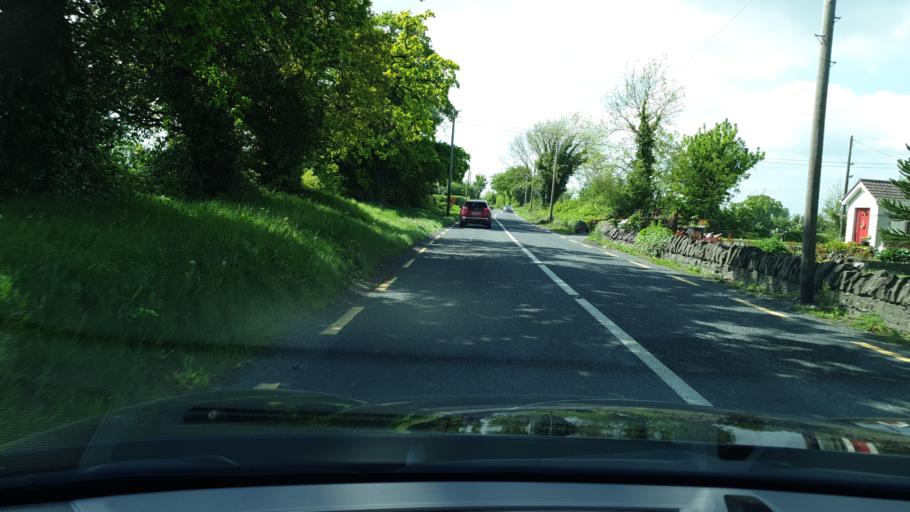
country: IE
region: Leinster
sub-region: An Mhi
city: Dunshaughlin
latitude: 53.5193
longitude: -6.5026
